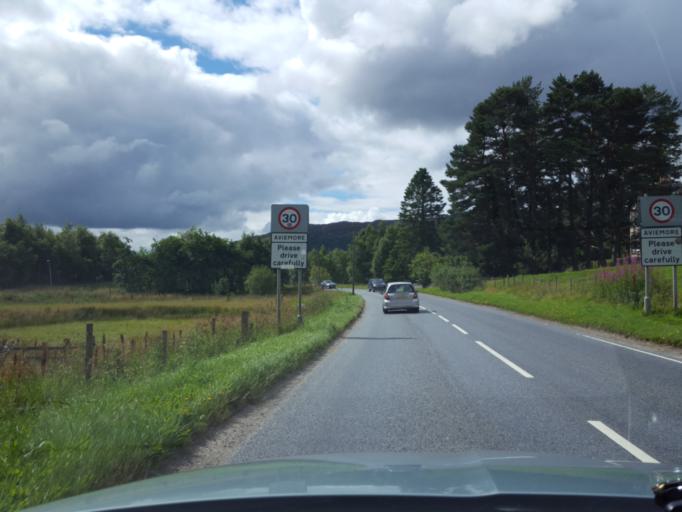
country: GB
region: Scotland
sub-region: Highland
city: Aviemore
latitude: 57.2069
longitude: -3.8258
